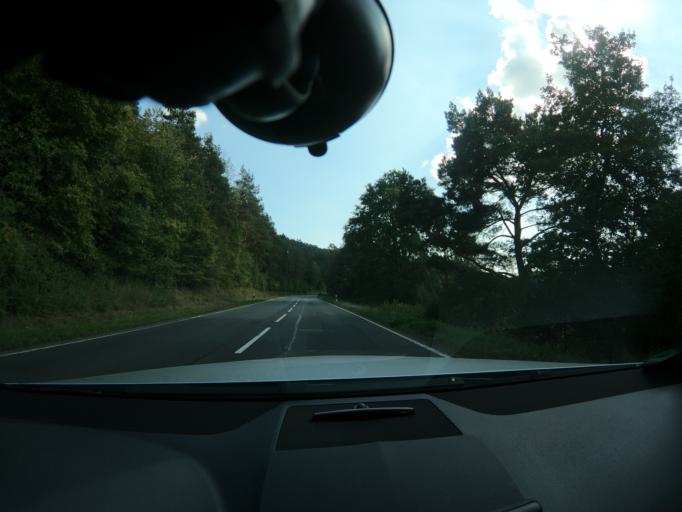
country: DE
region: Hesse
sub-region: Regierungsbezirk Giessen
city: Rauschenberg
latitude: 50.8737
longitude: 8.9364
